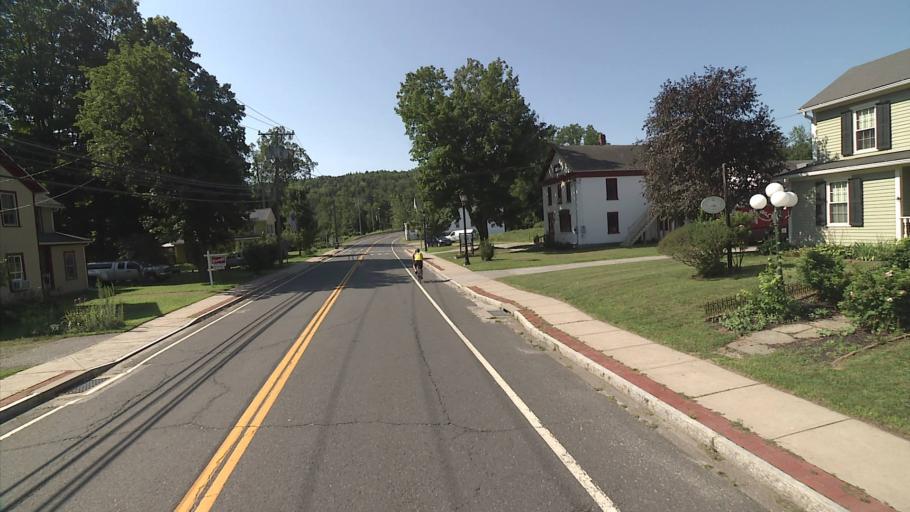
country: US
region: Connecticut
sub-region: Litchfield County
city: Winsted
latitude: 41.9615
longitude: -73.0195
